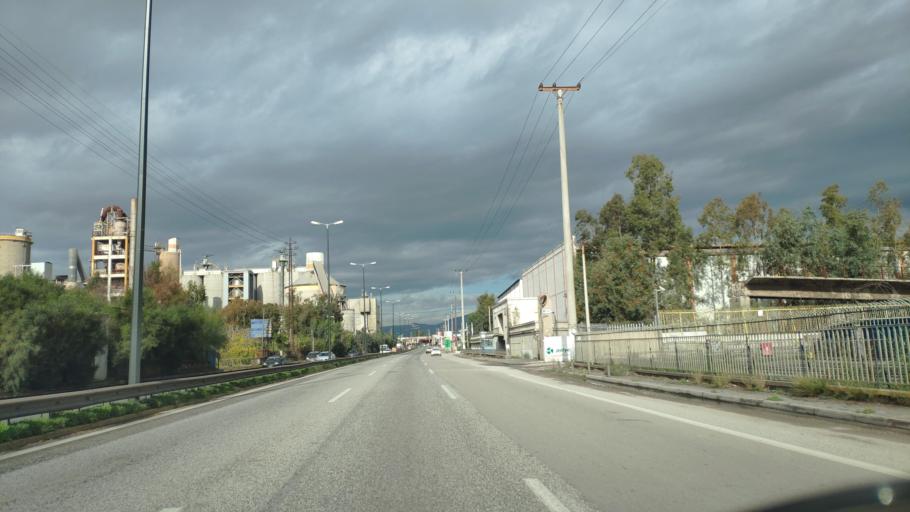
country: GR
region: Attica
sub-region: Nomarchia Athinas
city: Skaramangas
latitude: 38.0327
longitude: 23.5956
